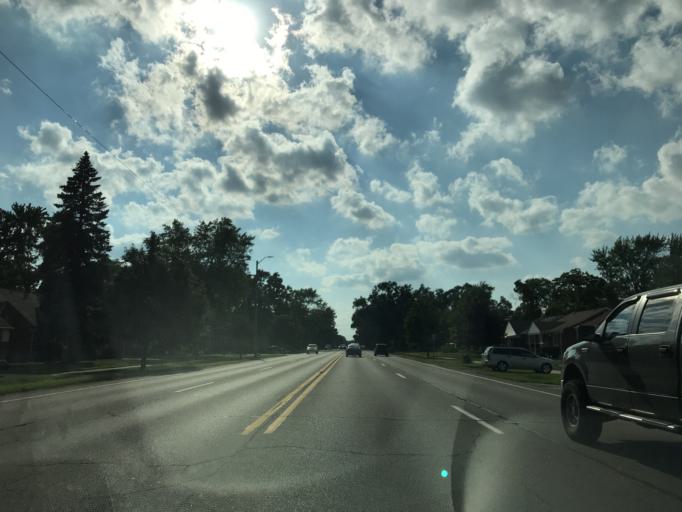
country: US
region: Michigan
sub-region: Wayne County
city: Redford
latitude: 42.3992
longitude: -83.3028
